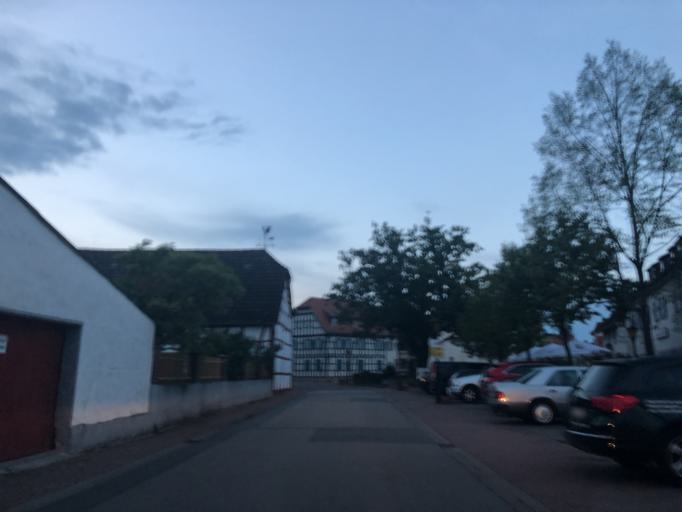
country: DE
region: Hesse
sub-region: Regierungsbezirk Darmstadt
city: Nauheim
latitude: 49.9628
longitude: 8.4501
